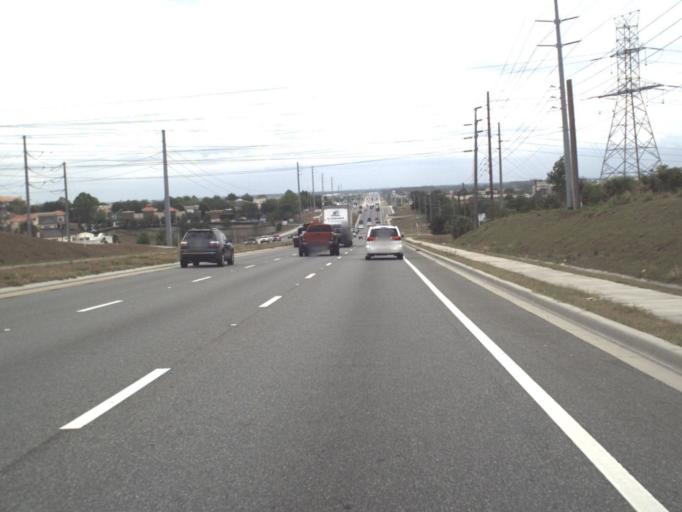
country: US
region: Florida
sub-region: Lake County
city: Minneola
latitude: 28.5466
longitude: -81.7141
